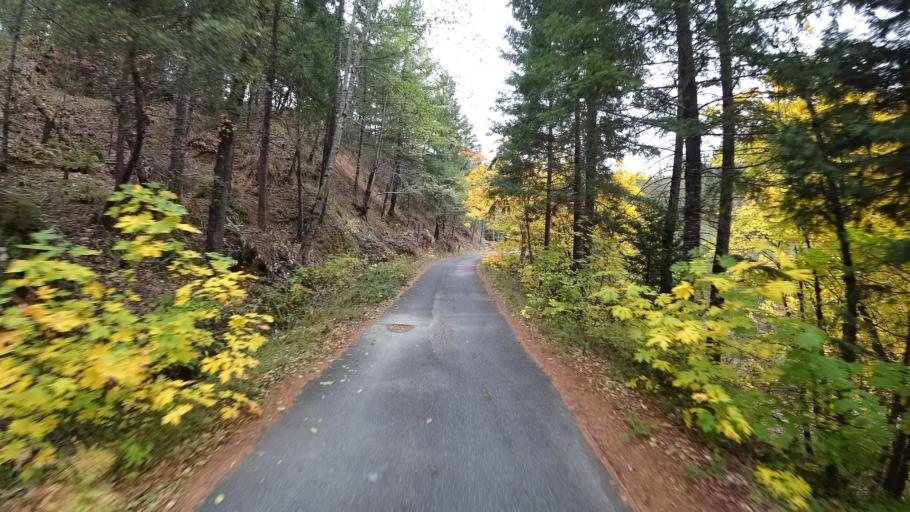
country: US
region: California
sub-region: Siskiyou County
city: Happy Camp
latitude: 41.7471
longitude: -123.3571
